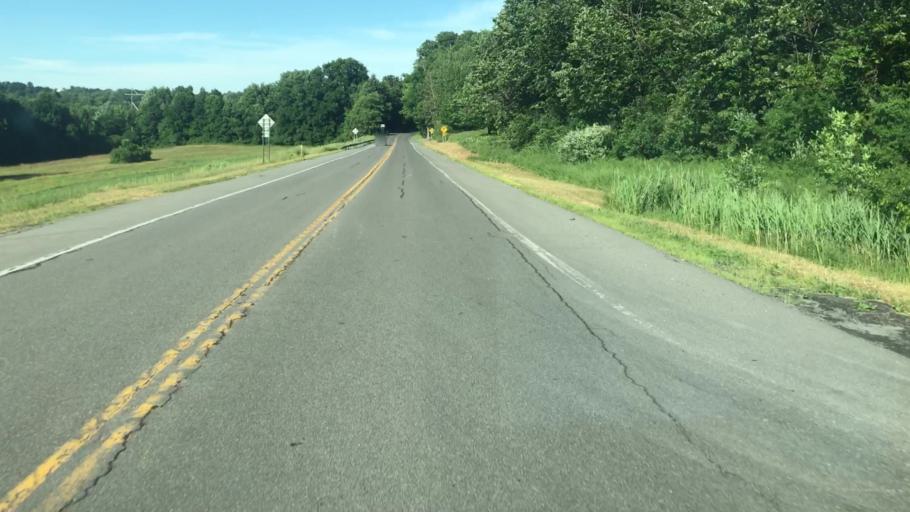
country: US
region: New York
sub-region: Onondaga County
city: Marcellus
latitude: 43.0191
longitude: -76.3750
